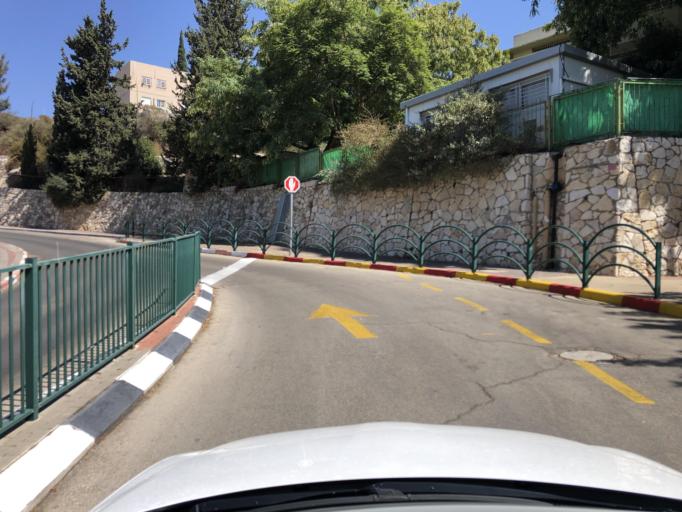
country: PS
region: West Bank
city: An Nabi Ilyas
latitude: 32.1718
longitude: 35.0128
